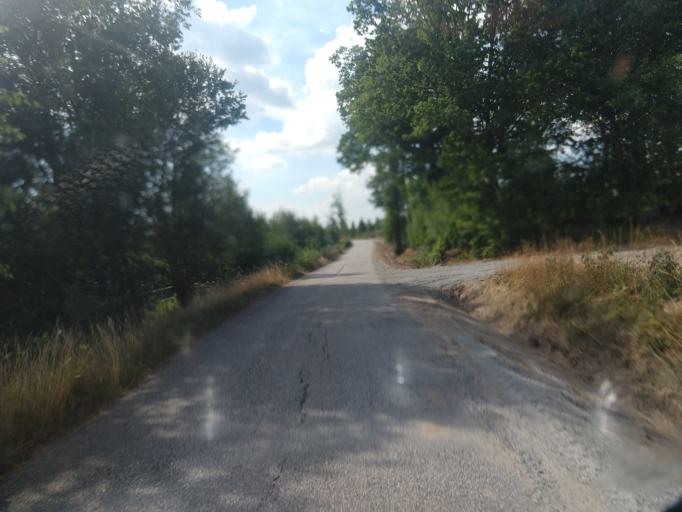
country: SE
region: Blekinge
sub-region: Karlskrona Kommun
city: Rodeby
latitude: 56.2445
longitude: 15.5562
